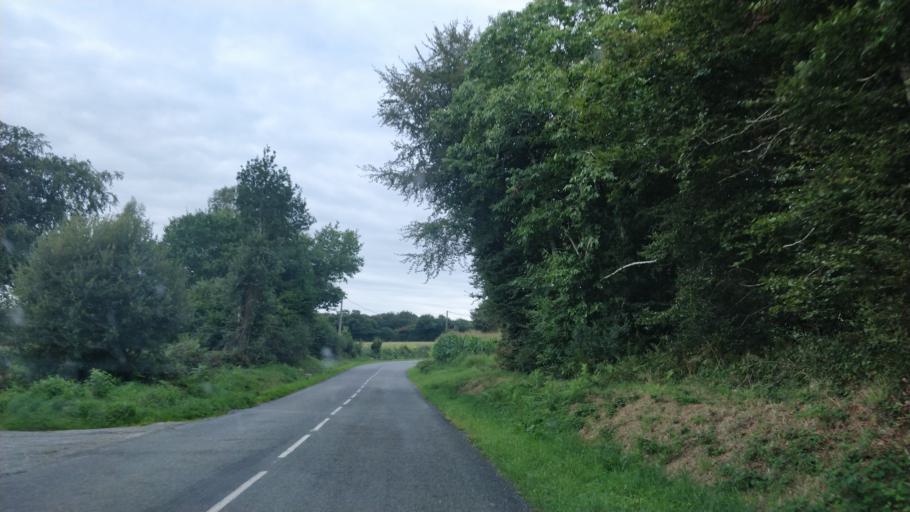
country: FR
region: Brittany
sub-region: Departement du Finistere
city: Loperhet
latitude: 48.3950
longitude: -4.3112
